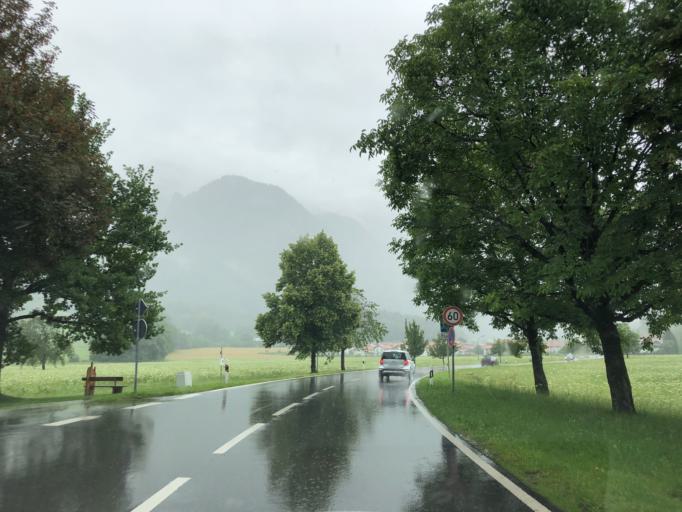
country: DE
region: Bavaria
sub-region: Upper Bavaria
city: Aschau im Chiemgau
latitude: 47.7719
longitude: 12.3256
